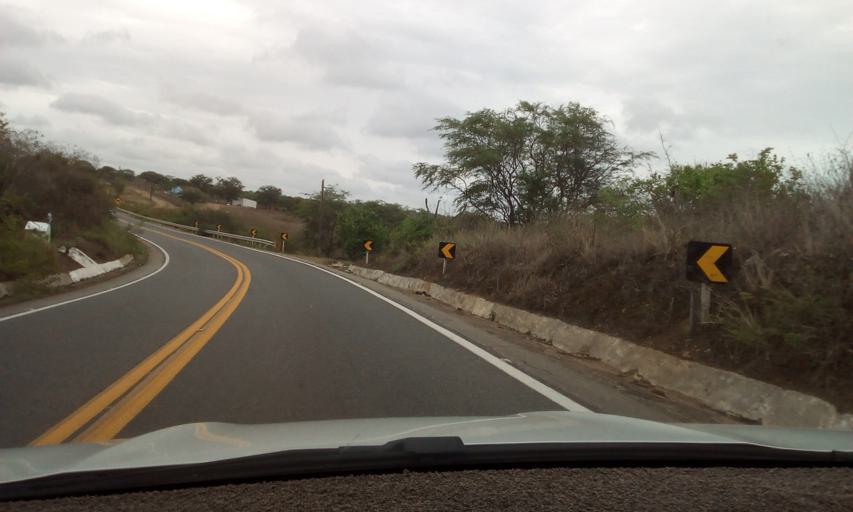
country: BR
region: Paraiba
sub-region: Areia
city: Remigio
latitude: -6.9572
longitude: -35.8058
